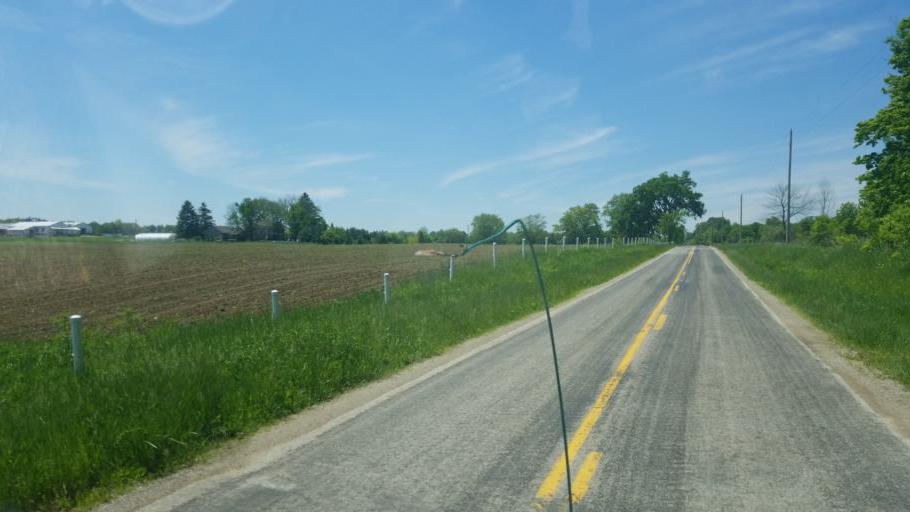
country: US
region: Ohio
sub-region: Huron County
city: Greenwich
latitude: 40.9679
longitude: -82.4155
